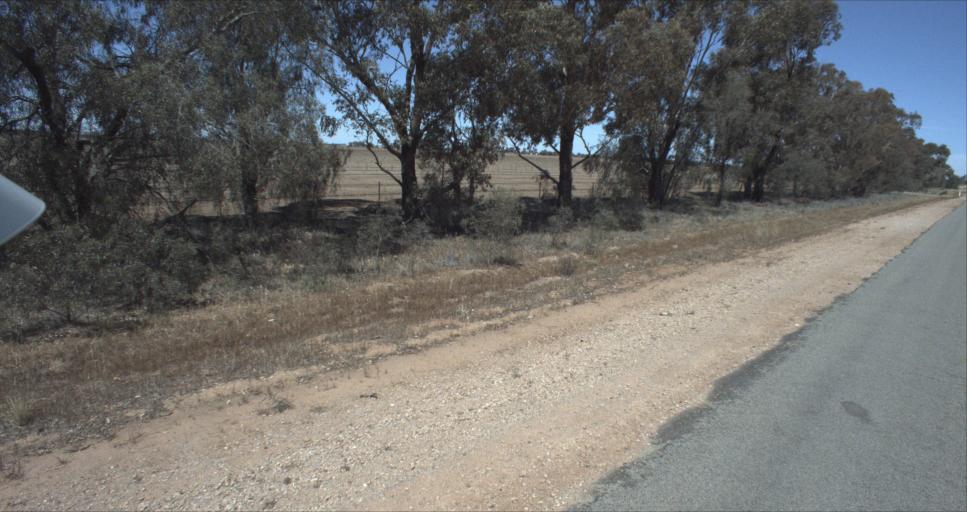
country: AU
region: New South Wales
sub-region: Leeton
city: Leeton
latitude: -34.5132
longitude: 146.3450
